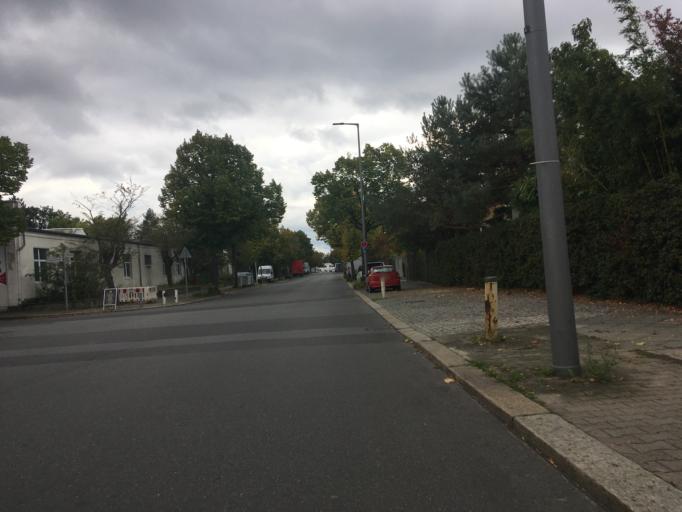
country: DE
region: Berlin
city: Tempelhof Bezirk
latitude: 52.4564
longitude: 13.3998
